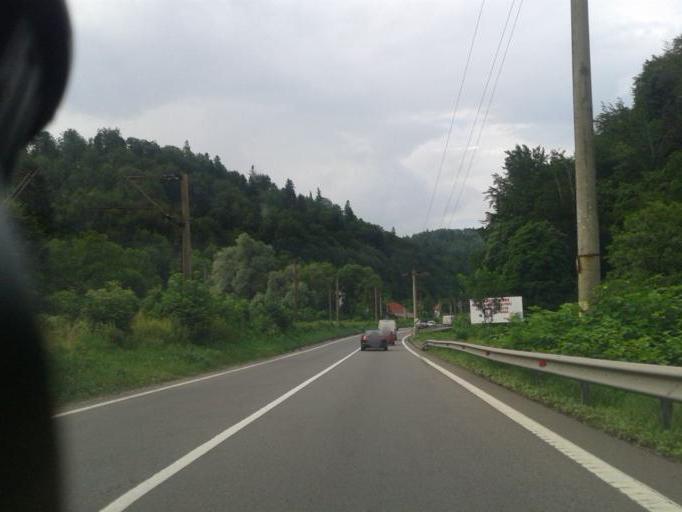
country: RO
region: Brasov
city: Brasov
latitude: 45.5817
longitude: 25.6217
